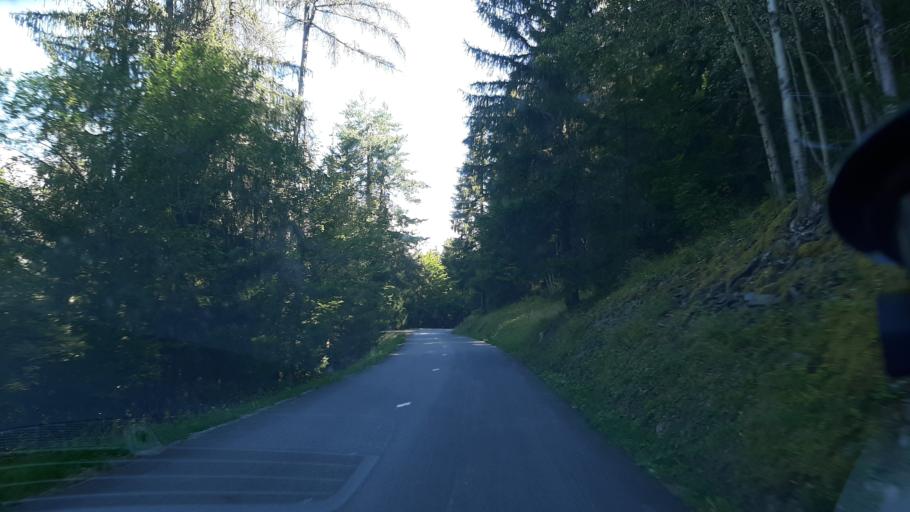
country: FR
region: Rhone-Alpes
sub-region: Departement de la Savoie
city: Aime
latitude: 45.5226
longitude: 6.6032
